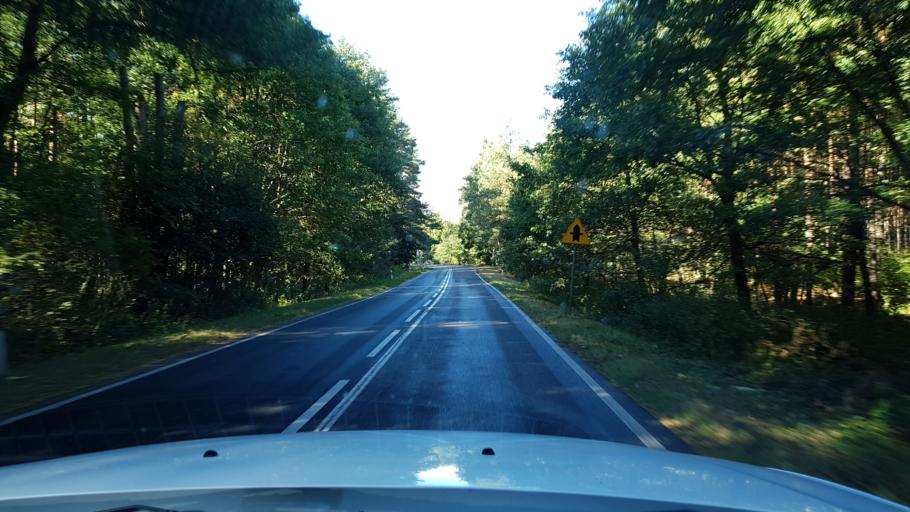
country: PL
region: West Pomeranian Voivodeship
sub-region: Powiat gryfinski
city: Gryfino
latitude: 53.1897
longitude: 14.5314
